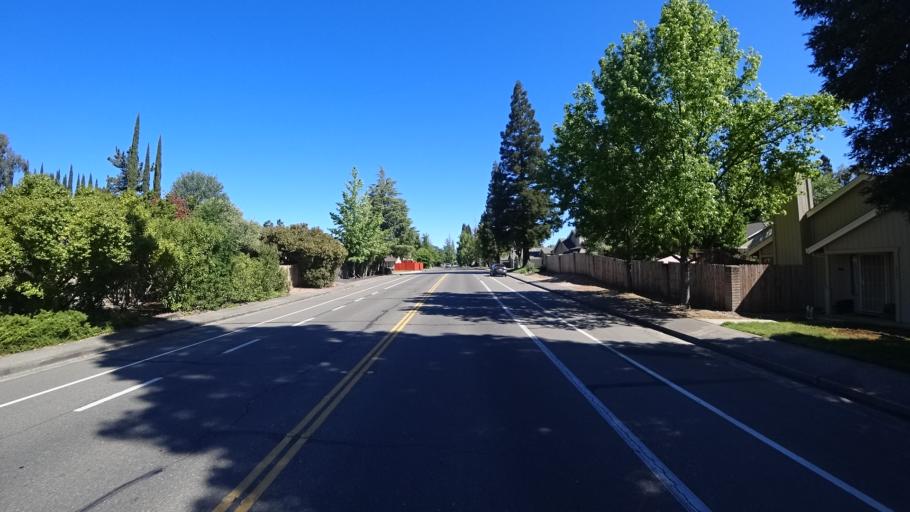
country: US
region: California
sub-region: Placer County
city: Rocklin
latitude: 38.7806
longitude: -121.2492
